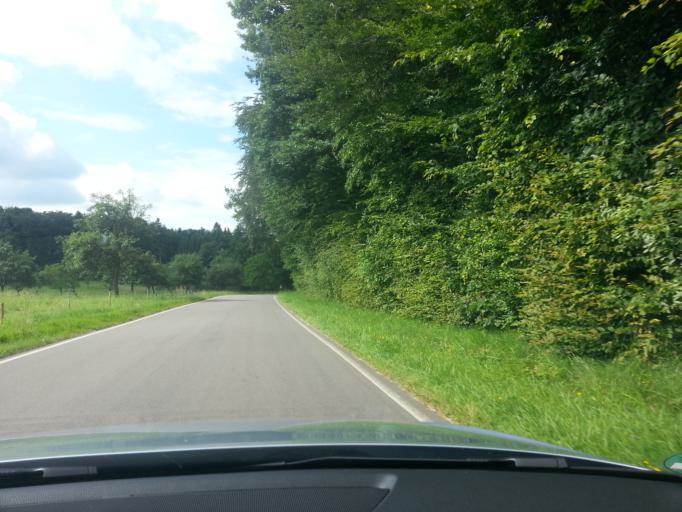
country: DE
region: Saarland
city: Weiten
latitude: 49.5259
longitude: 6.5248
